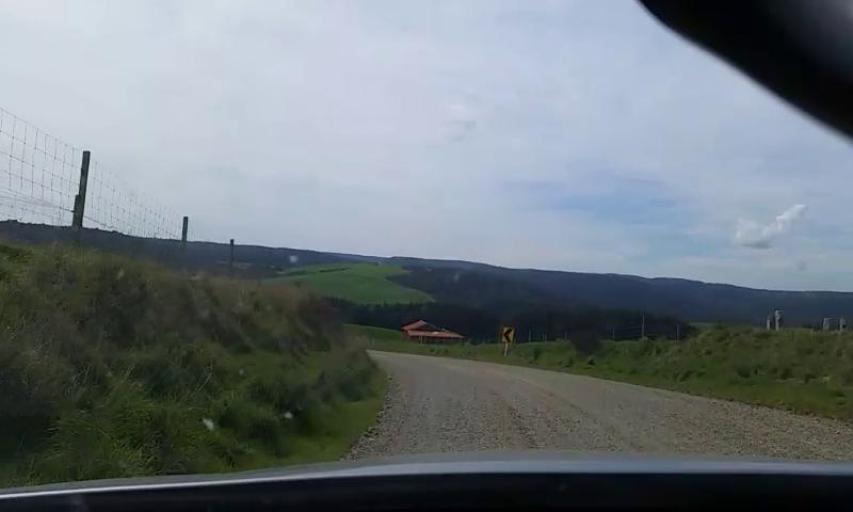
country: NZ
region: Otago
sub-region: Clutha District
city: Papatowai
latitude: -46.6306
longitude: 168.9821
